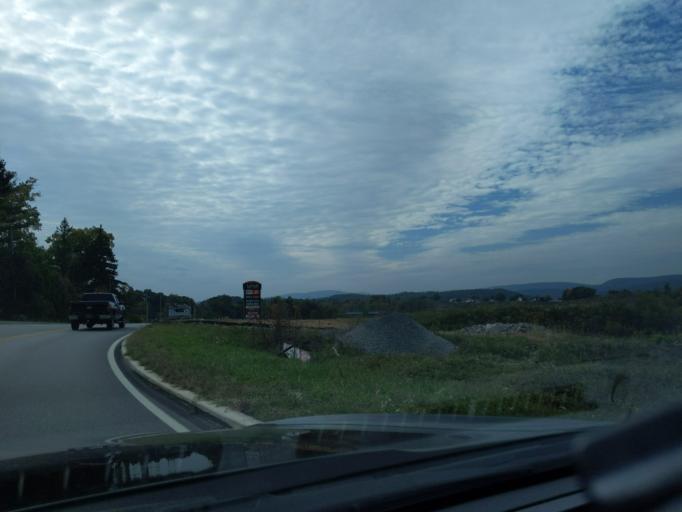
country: US
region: Pennsylvania
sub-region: Blair County
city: Lakemont
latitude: 40.4796
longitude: -78.3891
